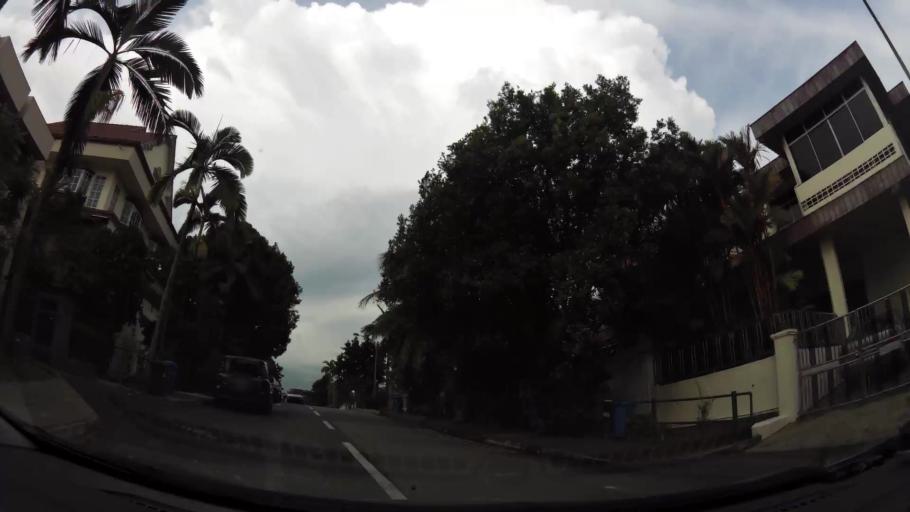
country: SG
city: Singapore
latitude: 1.3507
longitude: 103.8465
